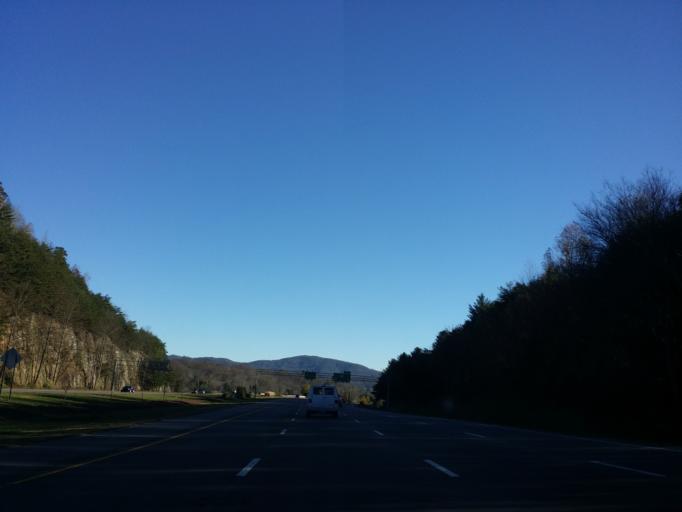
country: US
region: North Carolina
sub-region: Buncombe County
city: Asheville
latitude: 35.5889
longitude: -82.5264
